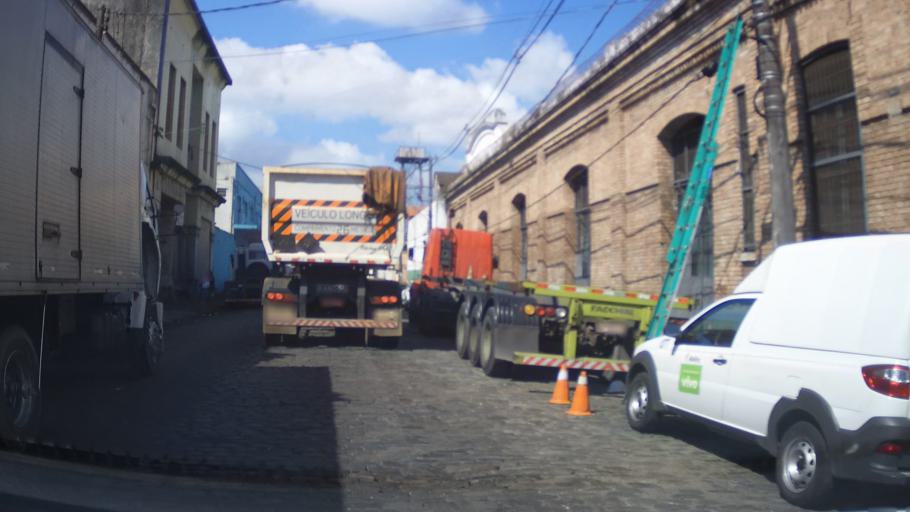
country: BR
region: Sao Paulo
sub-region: Santos
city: Santos
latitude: -23.9362
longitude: -46.3169
